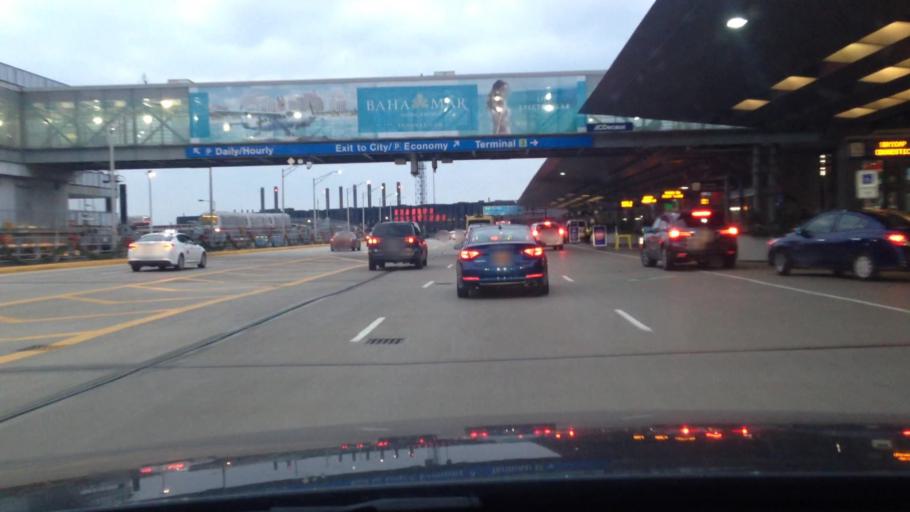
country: US
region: Illinois
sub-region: Cook County
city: Rosemont
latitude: 41.9768
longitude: -87.9019
